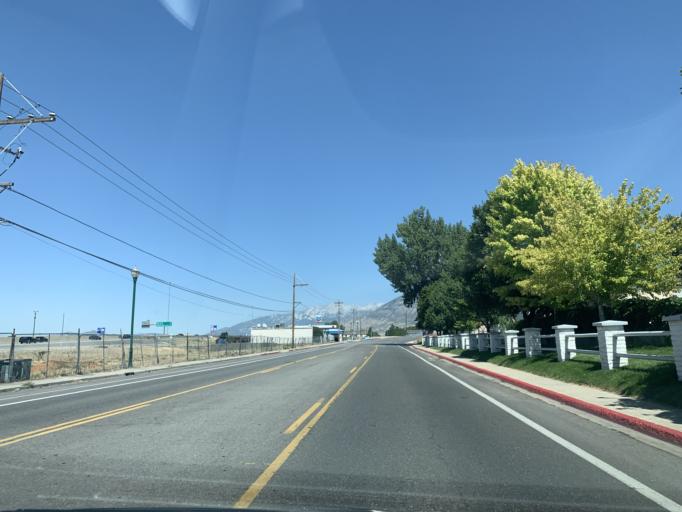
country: US
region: Utah
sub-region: Utah County
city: Orem
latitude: 40.2941
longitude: -111.7242
